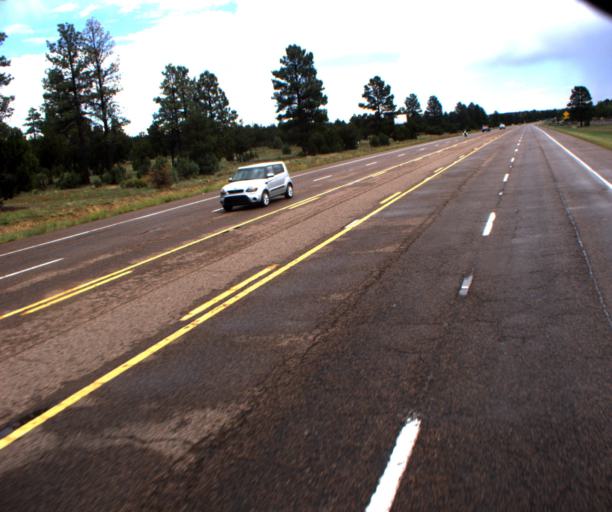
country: US
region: Arizona
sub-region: Navajo County
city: Heber-Overgaard
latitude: 34.3916
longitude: -110.5319
